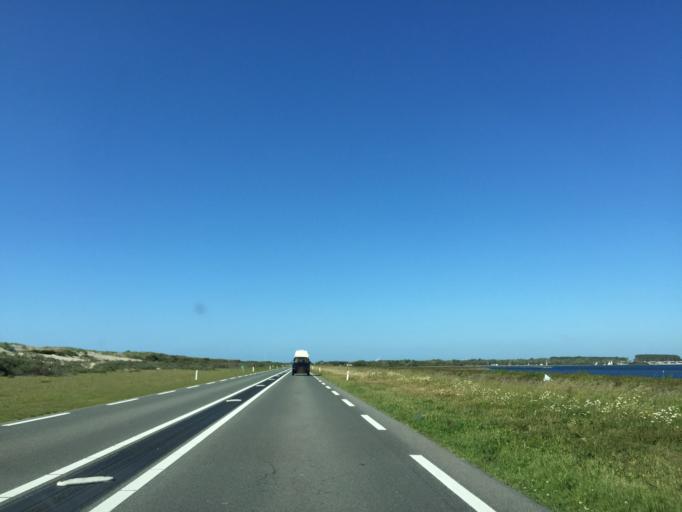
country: NL
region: Zeeland
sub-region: Schouwen-Duiveland
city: Scharendijke
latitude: 51.7705
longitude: 3.8619
